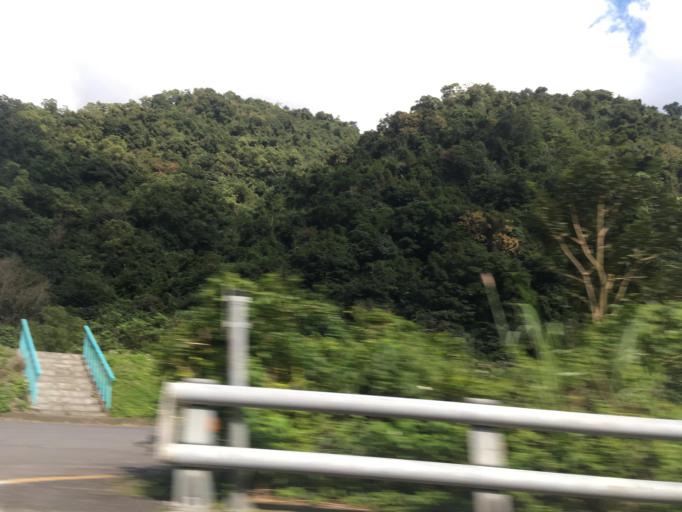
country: TW
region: Taiwan
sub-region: Yilan
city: Yilan
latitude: 24.7504
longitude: 121.6672
